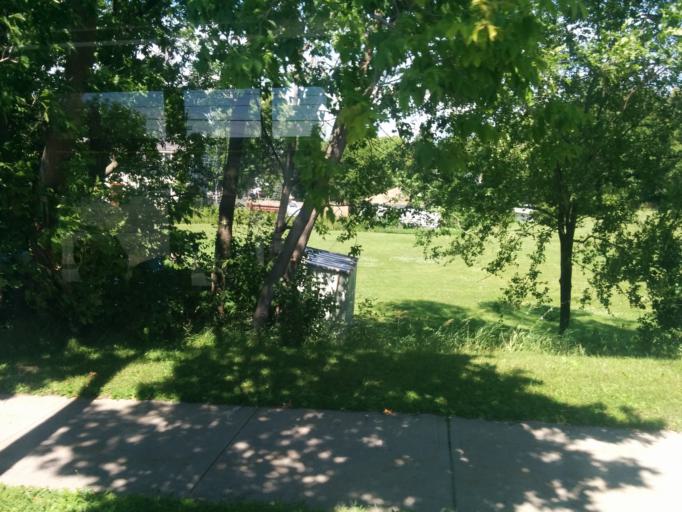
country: CA
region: Ontario
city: Kingston
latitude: 44.2493
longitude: -76.5288
